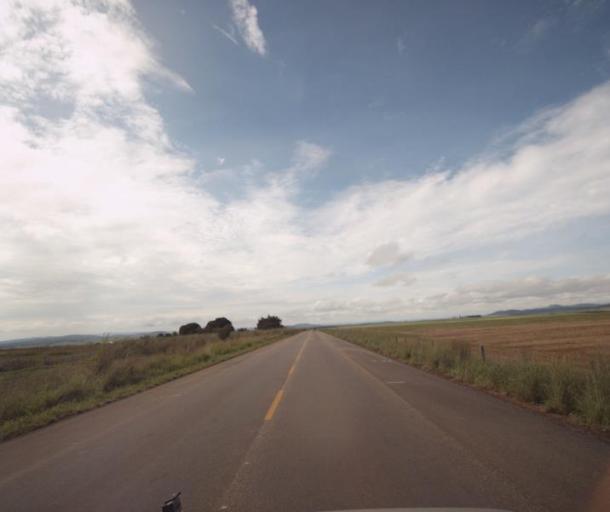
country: BR
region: Goias
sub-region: Padre Bernardo
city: Padre Bernardo
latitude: -15.3823
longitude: -48.6429
